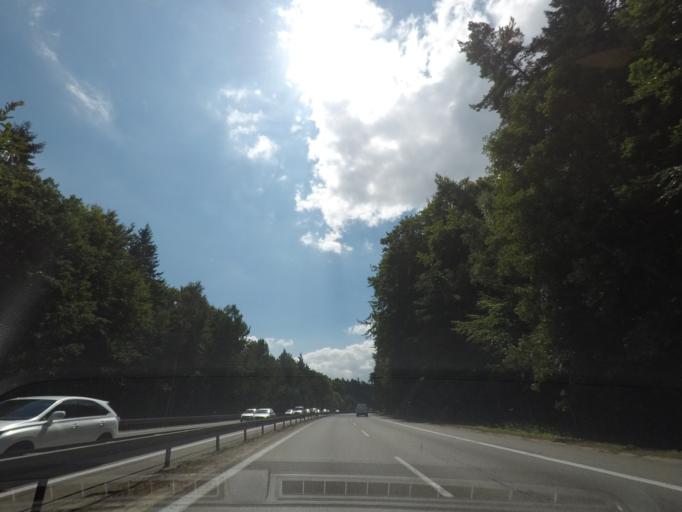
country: PL
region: Pomeranian Voivodeship
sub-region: Gdynia
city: Wielki Kack
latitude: 54.4527
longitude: 18.4924
